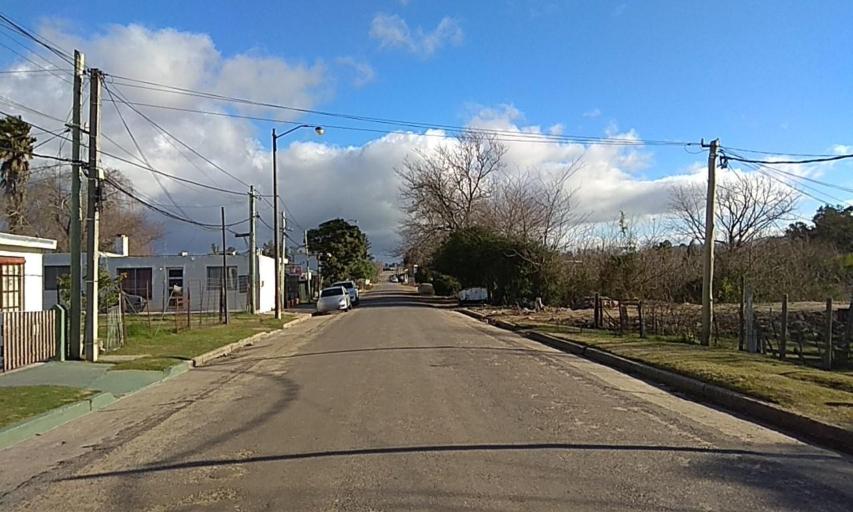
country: UY
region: Florida
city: Florida
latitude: -34.1054
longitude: -56.2206
